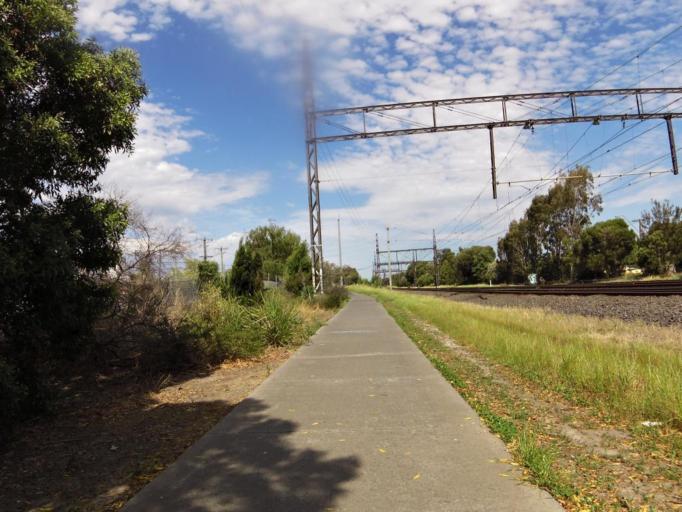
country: AU
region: Victoria
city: Hughesdale
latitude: -37.9046
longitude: 145.0940
